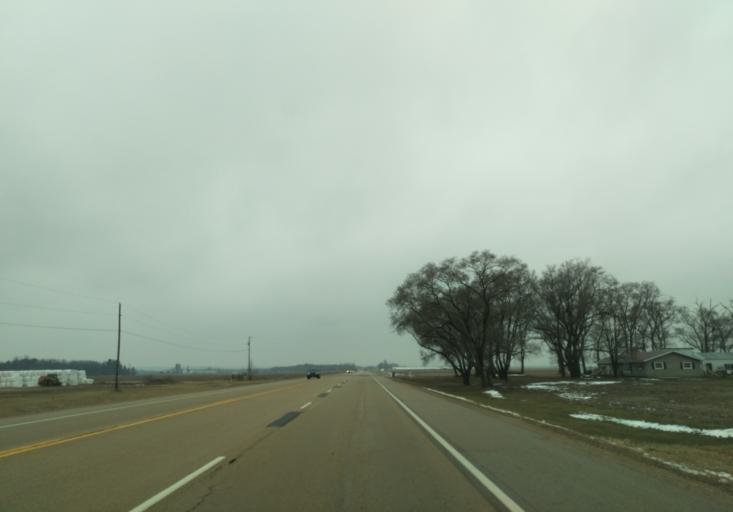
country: US
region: Wisconsin
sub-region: Sauk County
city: Spring Green
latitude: 43.1899
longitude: -90.1020
